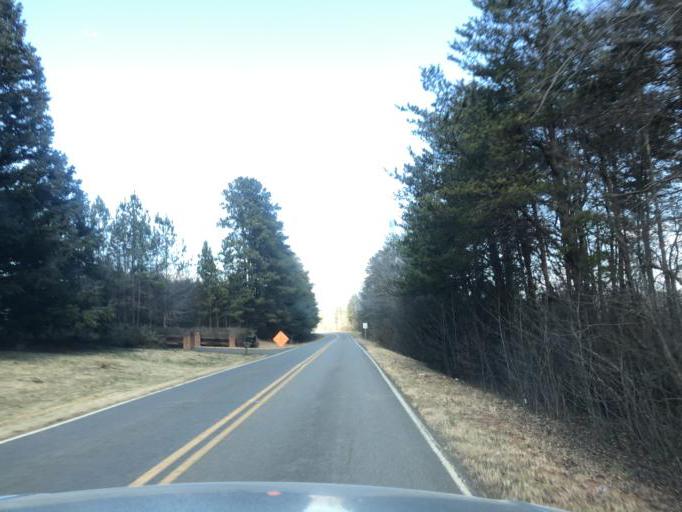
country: US
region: North Carolina
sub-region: Cleveland County
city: Shelby
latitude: 35.3212
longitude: -81.5383
